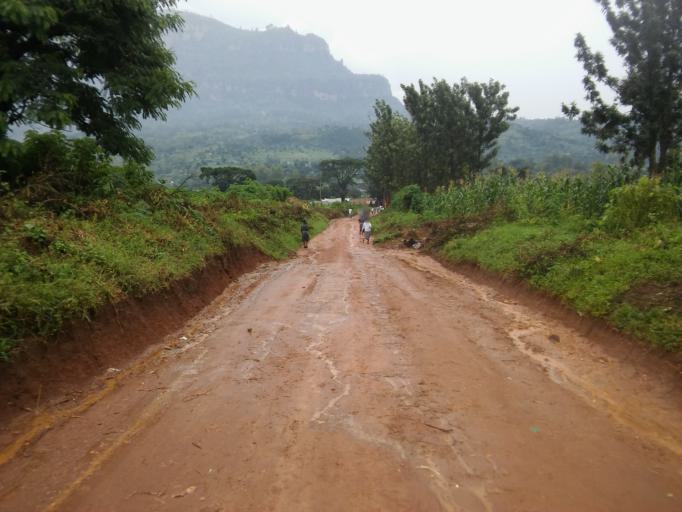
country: UG
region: Eastern Region
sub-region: Bududa District
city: Bududa
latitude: 0.9877
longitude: 34.2272
